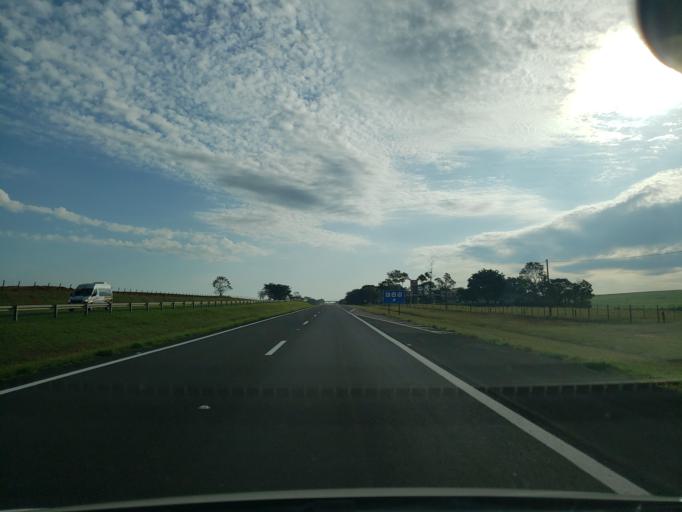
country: BR
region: Sao Paulo
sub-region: Valparaiso
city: Valparaiso
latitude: -21.2060
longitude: -50.7747
